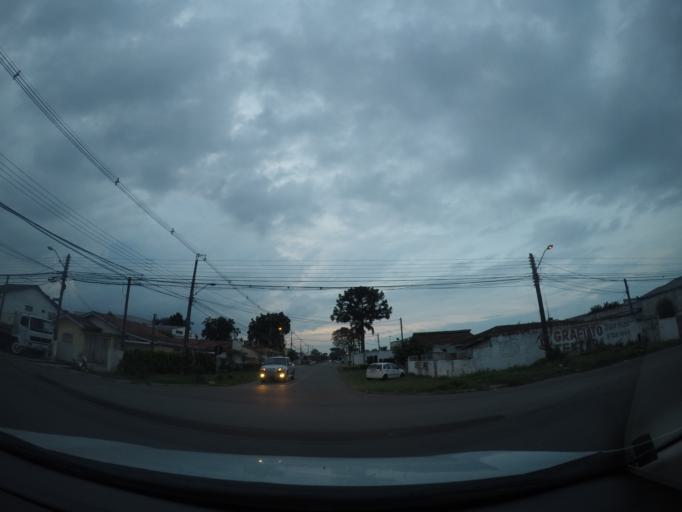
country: BR
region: Parana
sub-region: Sao Jose Dos Pinhais
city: Sao Jose dos Pinhais
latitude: -25.5077
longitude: -49.2262
